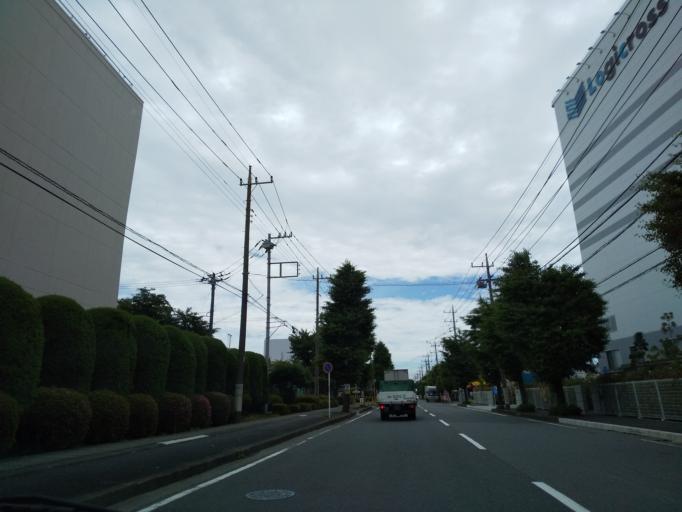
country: JP
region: Kanagawa
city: Zama
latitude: 35.5145
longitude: 139.3566
